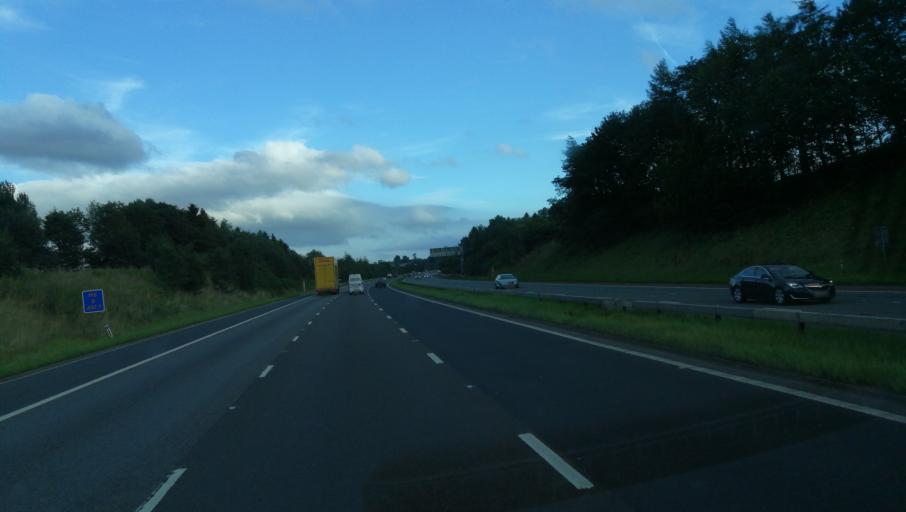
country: GB
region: England
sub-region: Cumbria
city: Penrith
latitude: 54.6449
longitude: -2.7404
